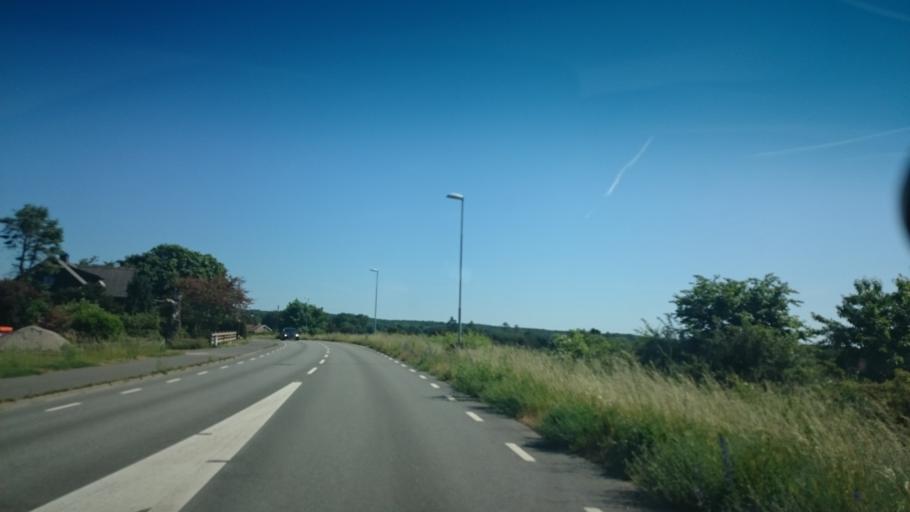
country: SE
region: Blekinge
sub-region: Solvesborgs Kommun
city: Soelvesborg
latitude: 56.0448
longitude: 14.5279
